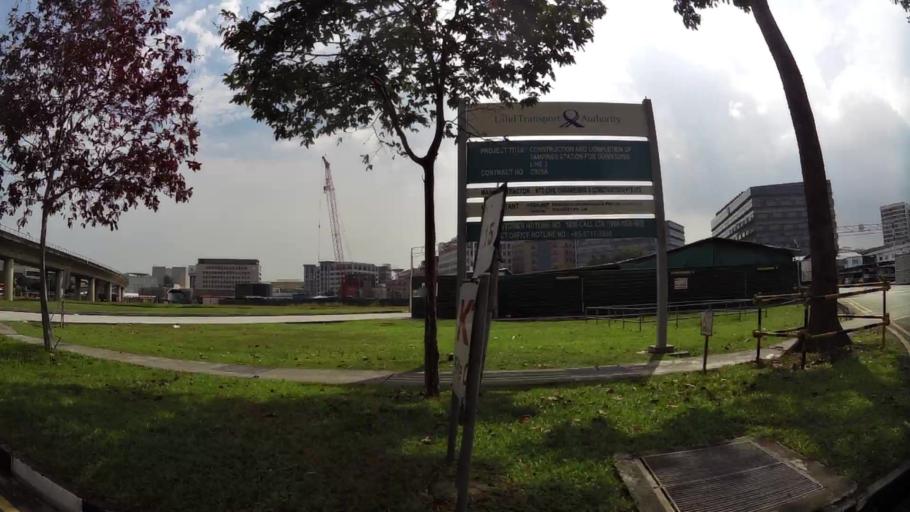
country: SG
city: Singapore
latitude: 1.3568
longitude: 103.9429
